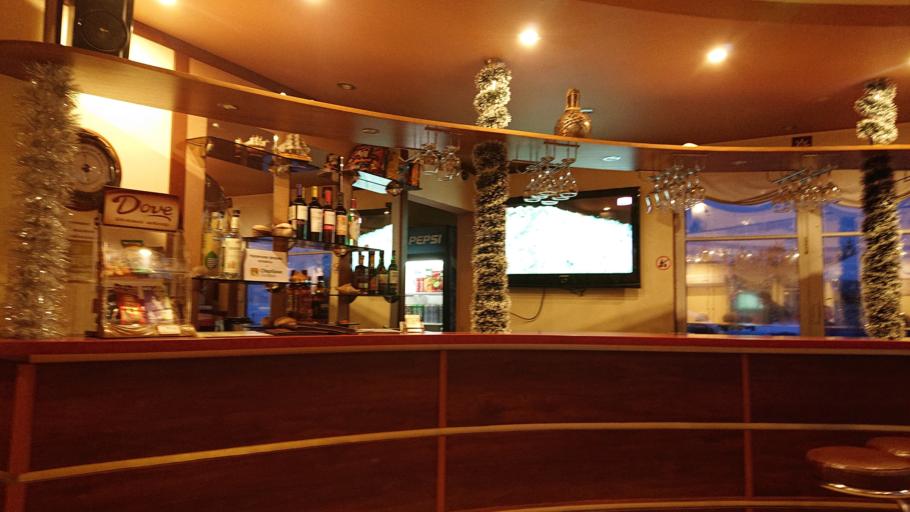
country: RU
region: Vologda
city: Sheksna
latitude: 59.2404
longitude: 38.5027
